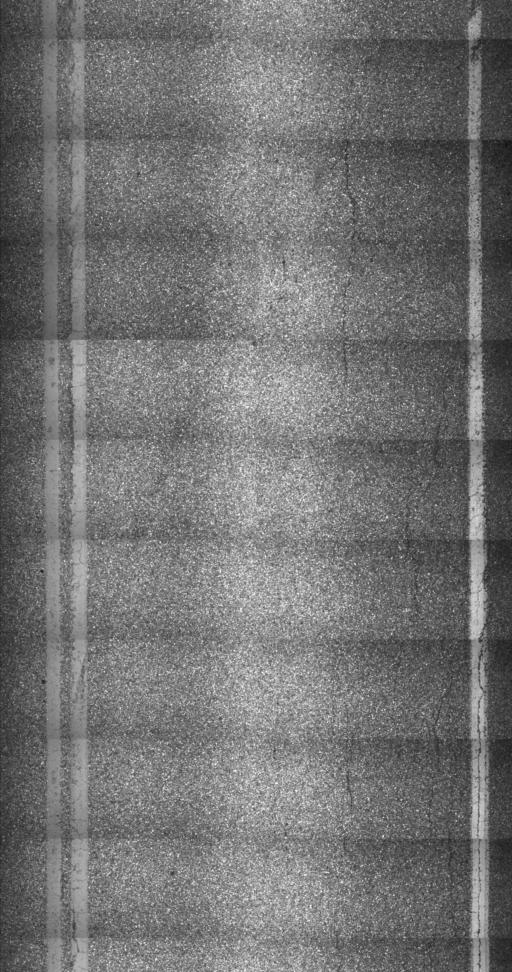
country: US
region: Vermont
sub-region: Bennington County
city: Manchester Center
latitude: 43.2585
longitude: -73.1022
